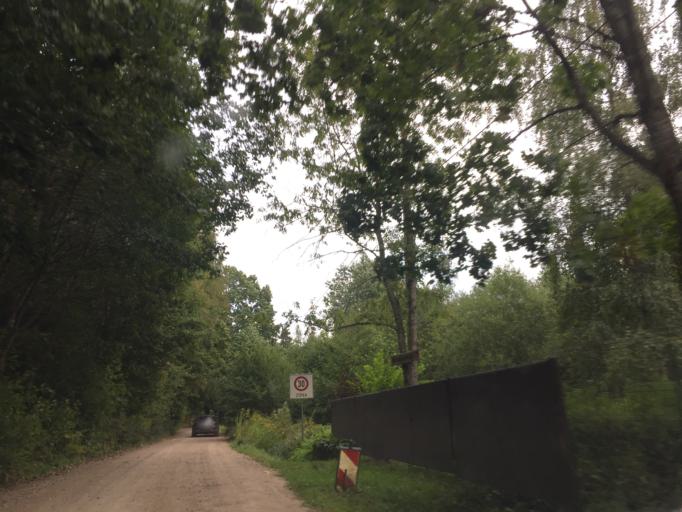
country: LV
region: Saulkrastu
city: Saulkrasti
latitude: 57.3350
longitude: 24.4163
